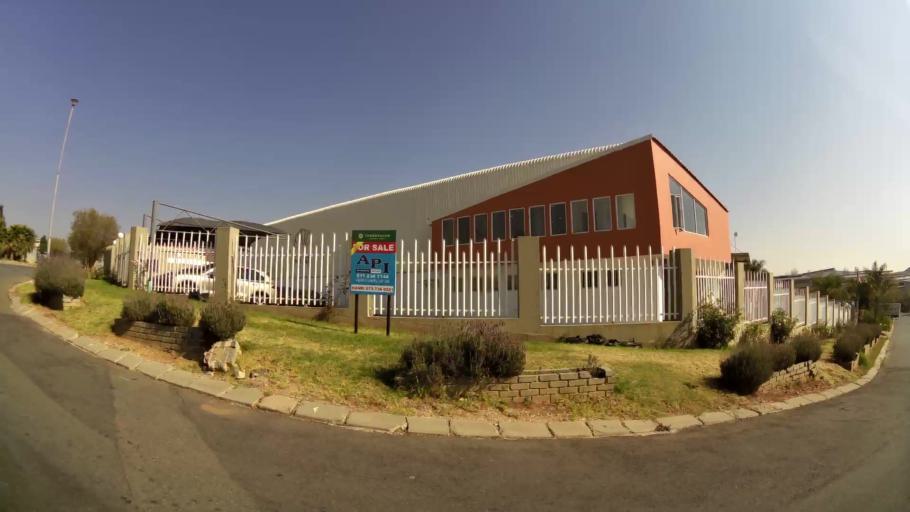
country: ZA
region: Gauteng
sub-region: City of Johannesburg Metropolitan Municipality
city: Modderfontein
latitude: -26.1121
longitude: 28.1408
